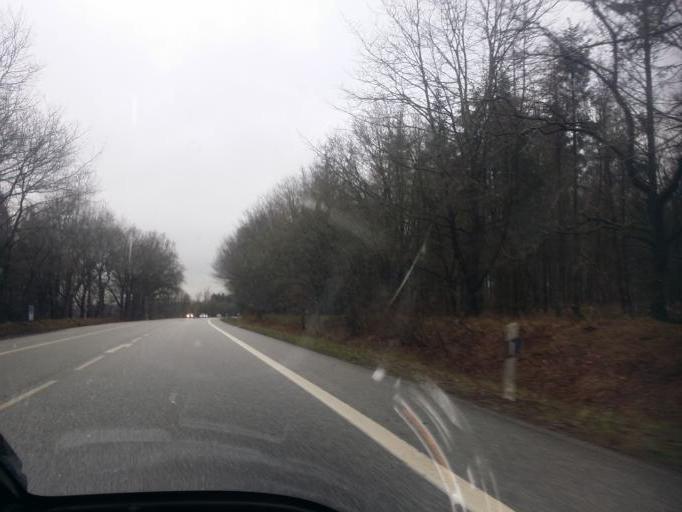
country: DE
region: Schleswig-Holstein
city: Bordelum
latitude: 54.6580
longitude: 8.9495
